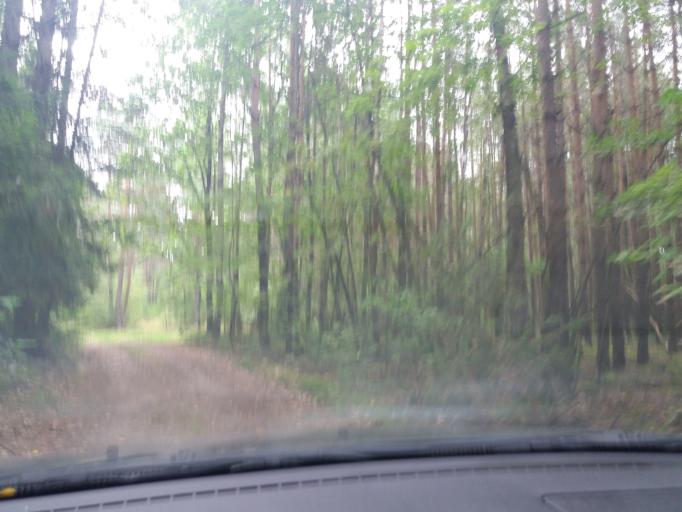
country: PL
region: Masovian Voivodeship
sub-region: Powiat mlawski
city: Wieczfnia Koscielna
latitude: 53.2283
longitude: 20.4726
